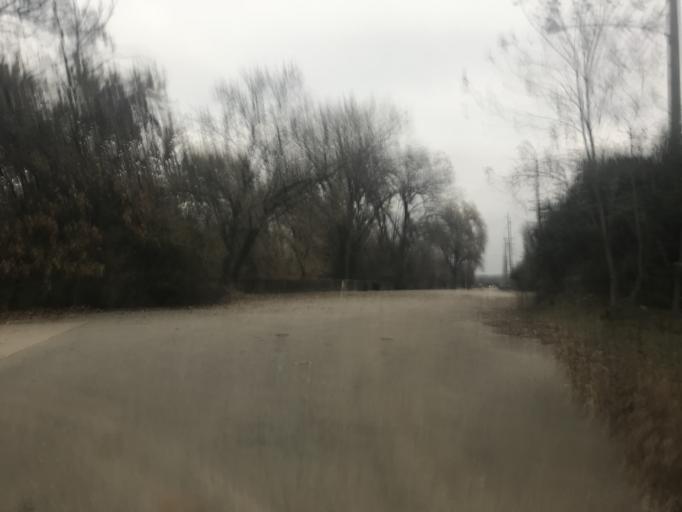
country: US
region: Indiana
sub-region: Clark County
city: Jeffersonville
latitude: 38.2662
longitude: -85.7219
